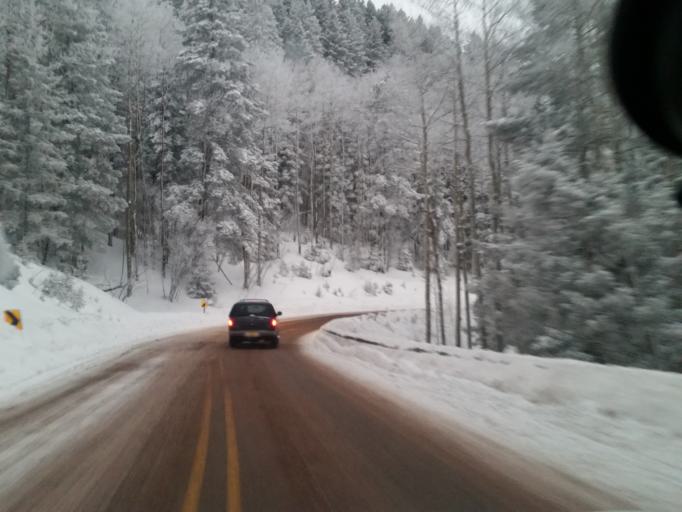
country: US
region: New Mexico
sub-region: Santa Fe County
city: Santa Fe
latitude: 35.7606
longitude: -105.8140
